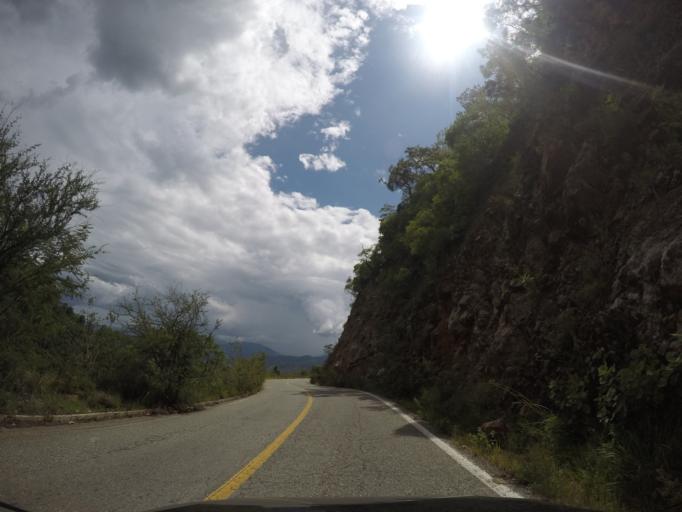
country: MX
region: Oaxaca
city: San Francisco Sola
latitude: 16.4323
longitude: -97.0407
